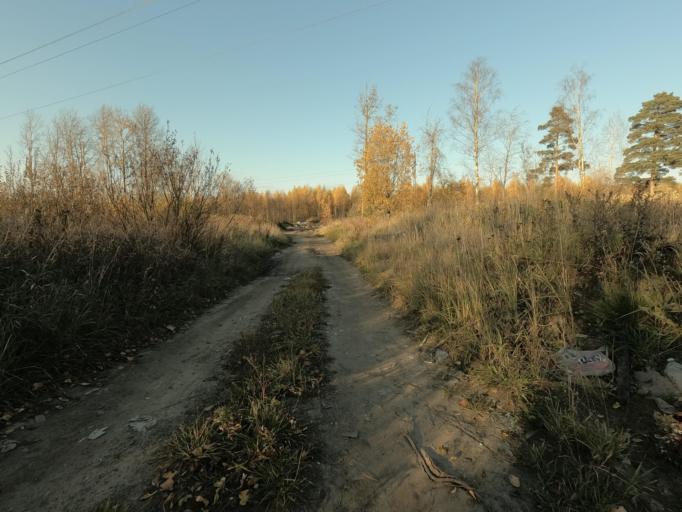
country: RU
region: Leningrad
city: Kirovsk
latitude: 59.8621
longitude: 31.0122
